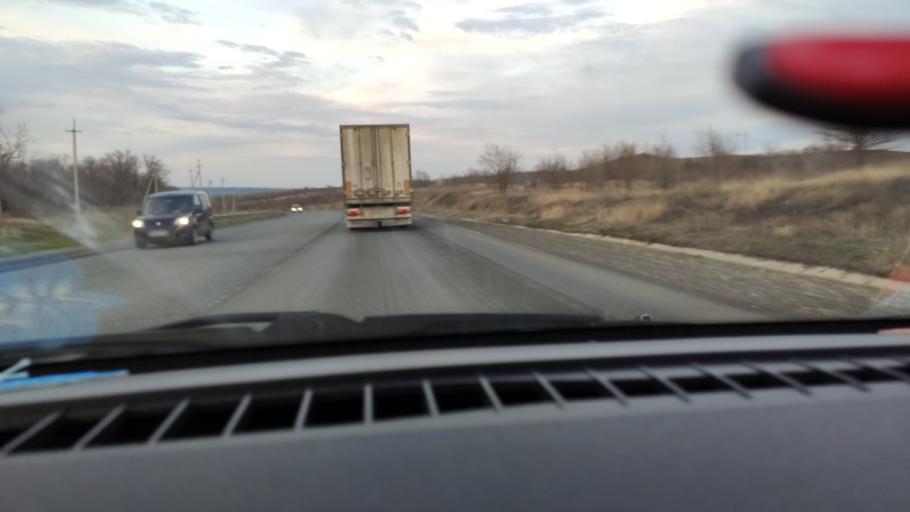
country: RU
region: Saratov
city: Shumeyka
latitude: 51.7799
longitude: 46.1232
